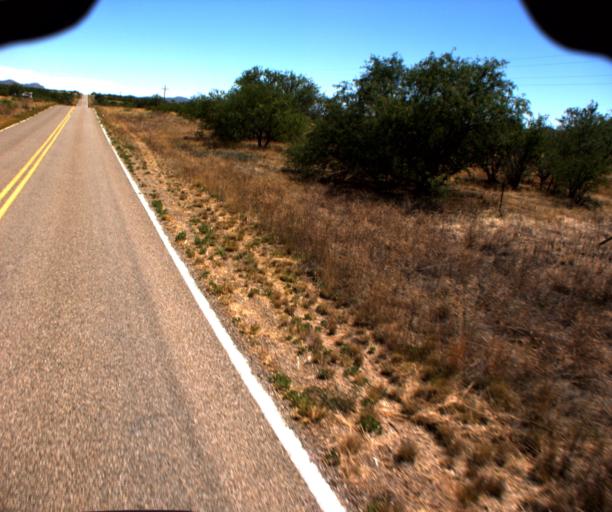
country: US
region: Arizona
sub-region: Pima County
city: Sells
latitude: 31.5636
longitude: -111.5386
